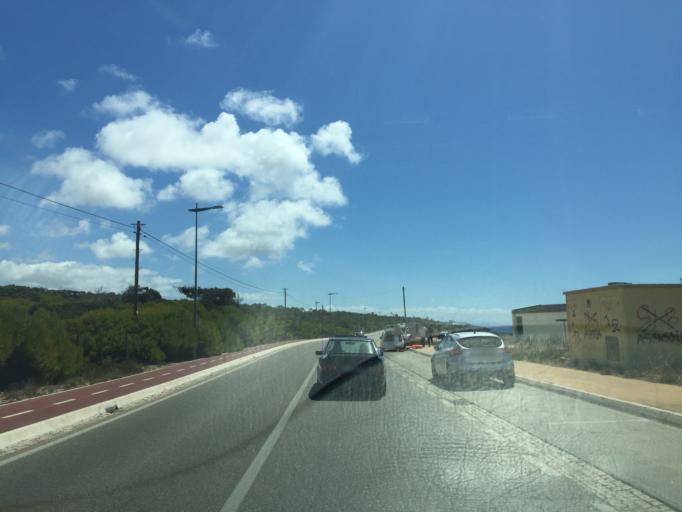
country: PT
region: Lisbon
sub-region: Cascais
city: Cascais
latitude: 38.7031
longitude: -9.4764
